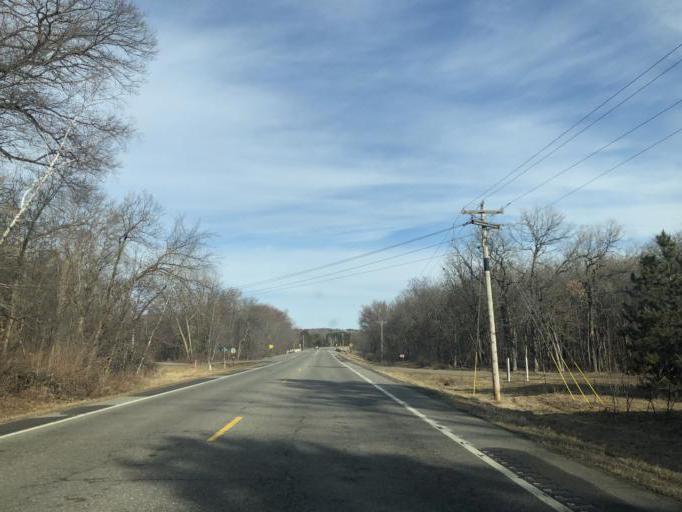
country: US
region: Minnesota
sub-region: Sherburne County
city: Becker
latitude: 45.4235
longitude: -93.8739
